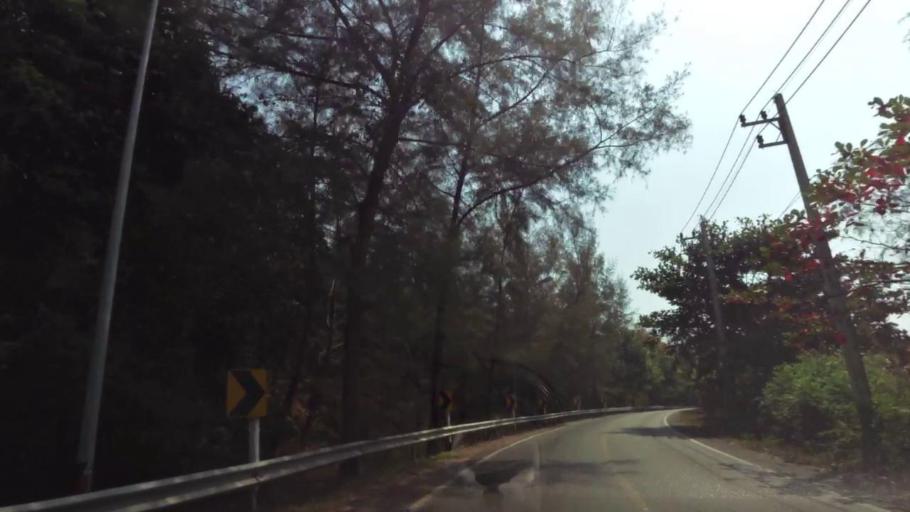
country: TH
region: Chanthaburi
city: Tha Mai
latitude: 12.5318
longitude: 101.9451
